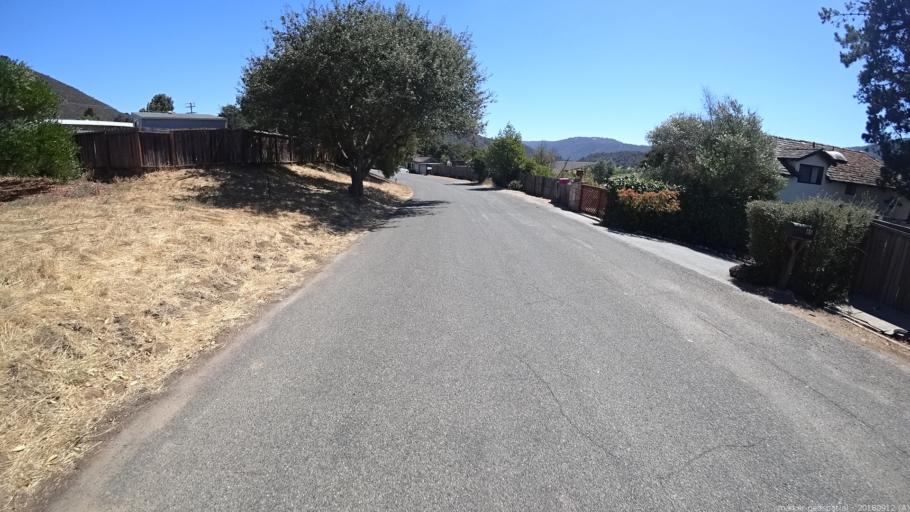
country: US
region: California
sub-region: Monterey County
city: Carmel Valley Village
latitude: 36.4775
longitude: -121.7232
